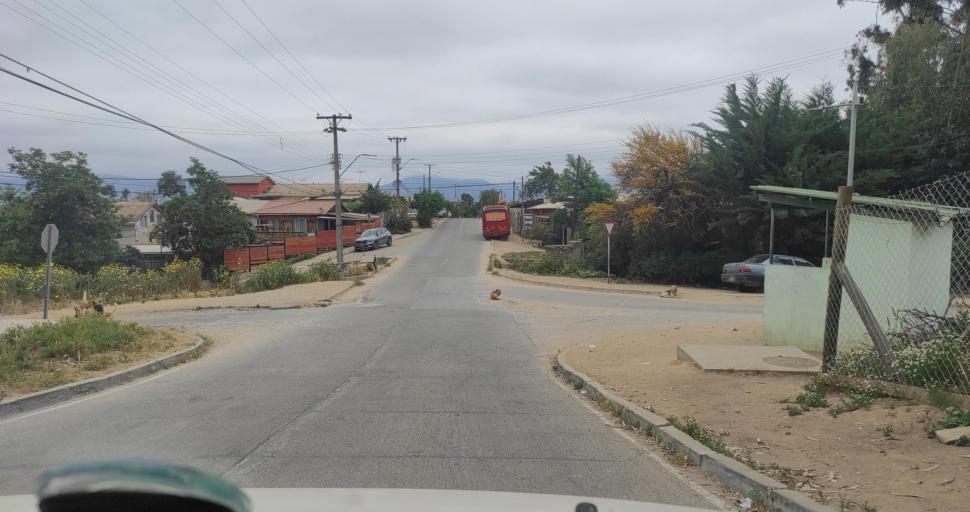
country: CL
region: Valparaiso
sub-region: Provincia de Marga Marga
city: Limache
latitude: -32.9883
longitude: -71.2250
